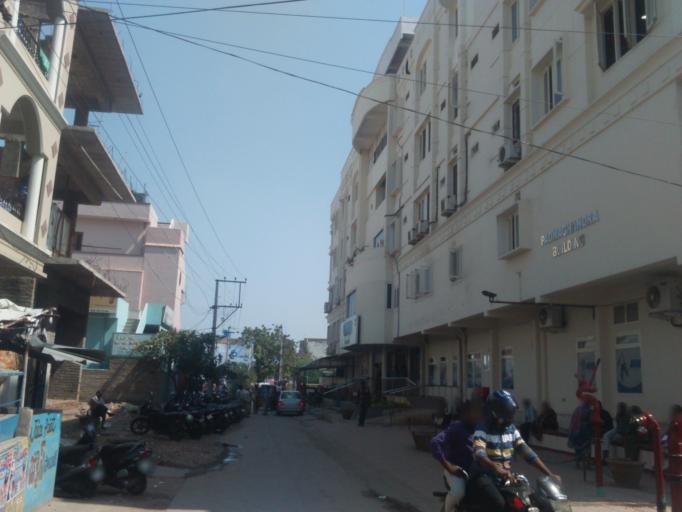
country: IN
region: Telangana
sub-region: Mahbubnagar
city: Alampur
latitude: 15.8235
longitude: 78.0412
